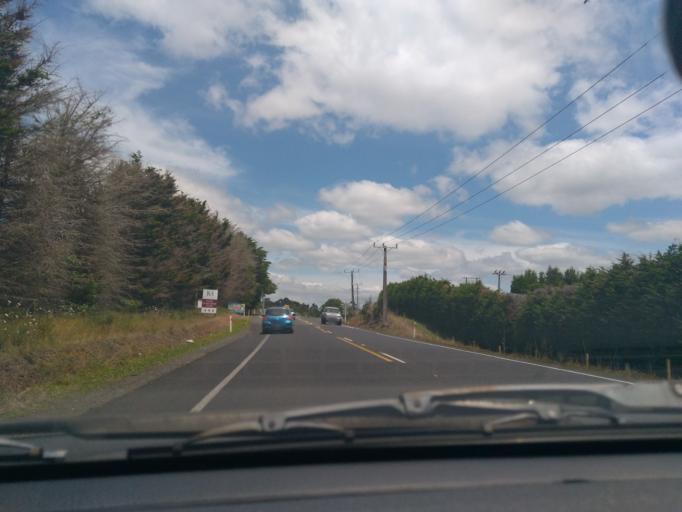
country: NZ
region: Northland
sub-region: Far North District
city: Kerikeri
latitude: -35.1900
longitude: 173.9107
